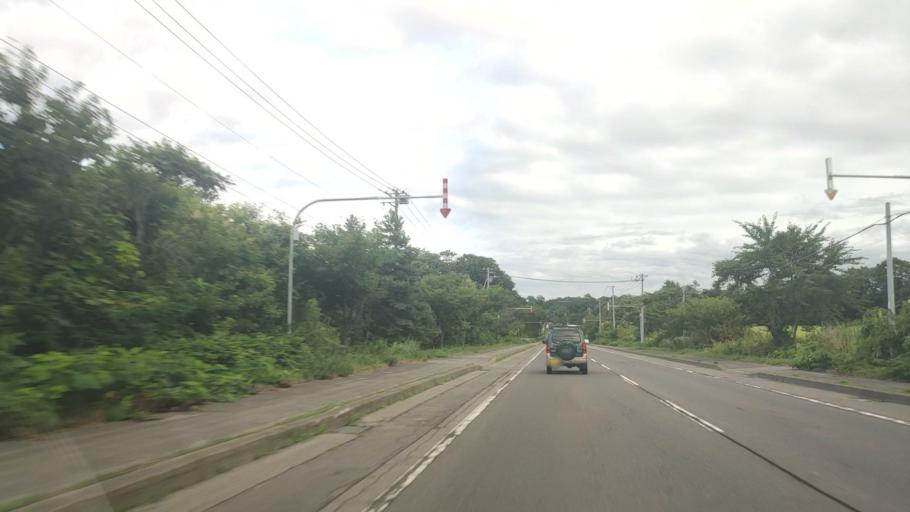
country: JP
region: Hokkaido
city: Nanae
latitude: 42.0874
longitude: 140.5830
